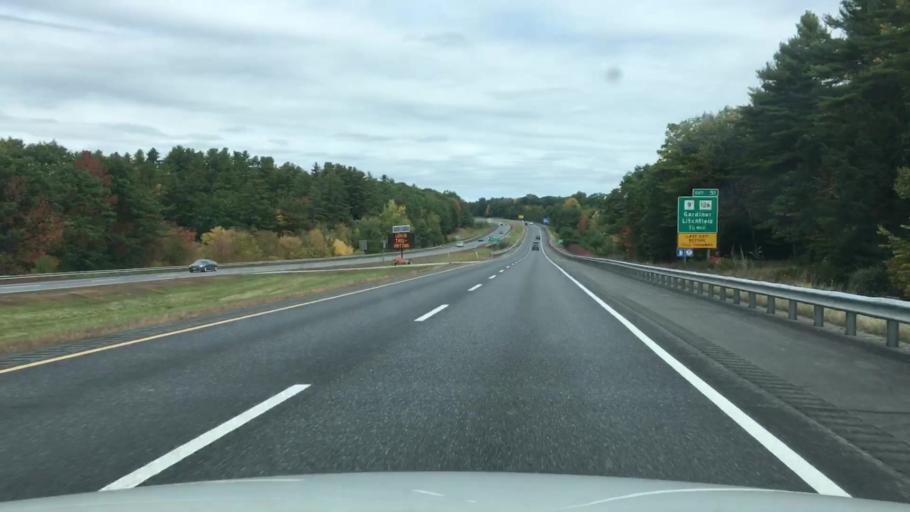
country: US
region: Maine
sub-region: Kennebec County
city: Gardiner
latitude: 44.1898
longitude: -69.8292
